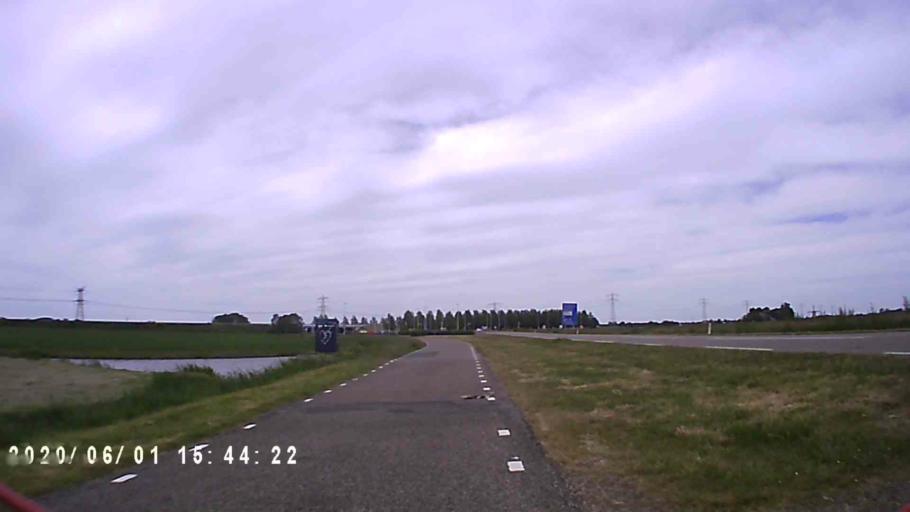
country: NL
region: Friesland
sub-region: Gemeente Boarnsterhim
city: Wergea
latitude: 53.1632
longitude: 5.8292
